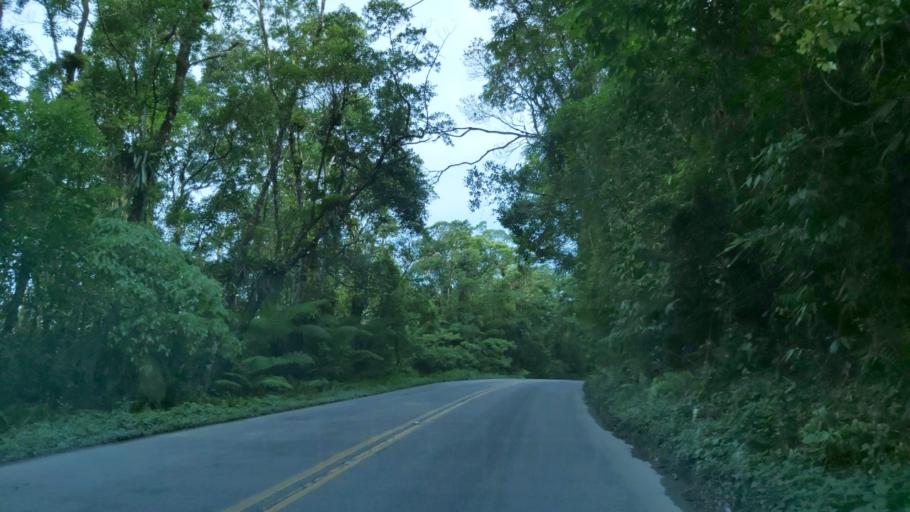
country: BR
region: Sao Paulo
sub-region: Miracatu
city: Miracatu
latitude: -24.0383
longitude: -47.5670
